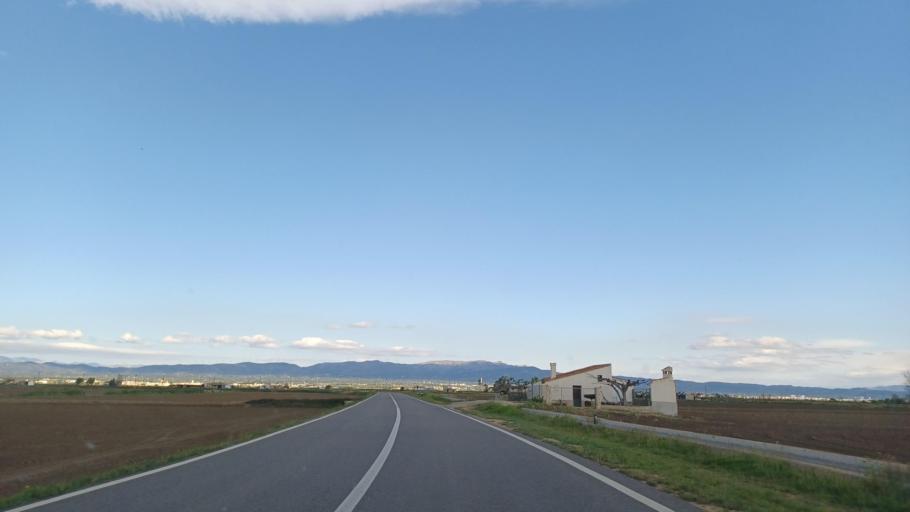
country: ES
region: Catalonia
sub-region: Provincia de Tarragona
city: Deltebre
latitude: 40.7473
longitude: 0.7107
